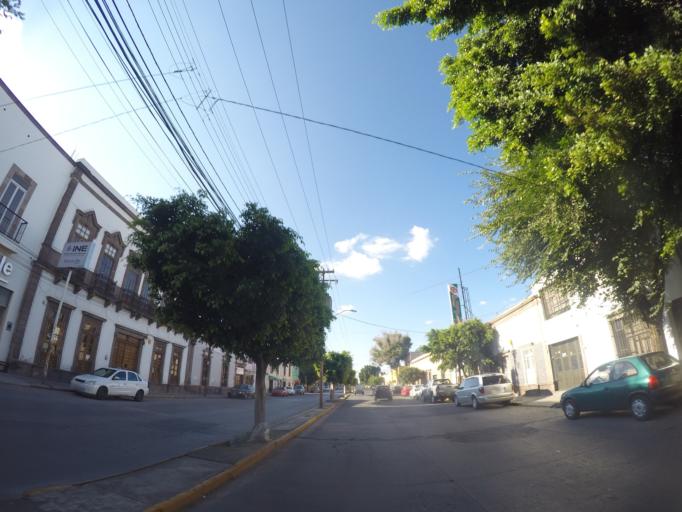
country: MX
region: San Luis Potosi
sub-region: San Luis Potosi
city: San Luis Potosi
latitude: 22.1581
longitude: -100.9797
